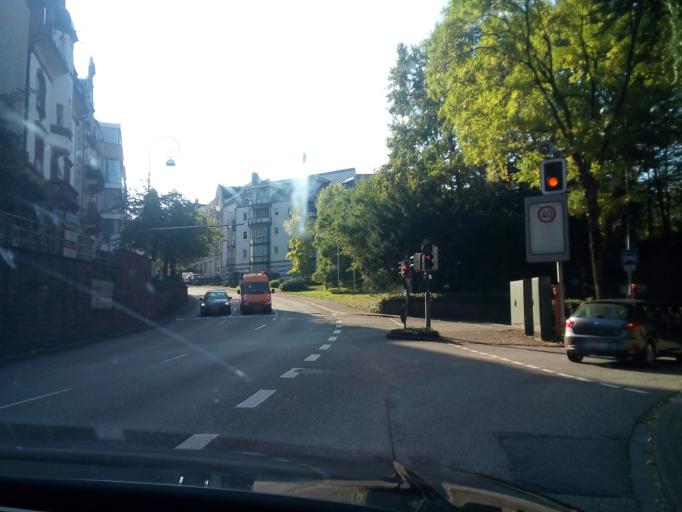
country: DE
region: Baden-Wuerttemberg
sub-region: Karlsruhe Region
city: Baden-Baden
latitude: 48.7539
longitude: 8.2449
